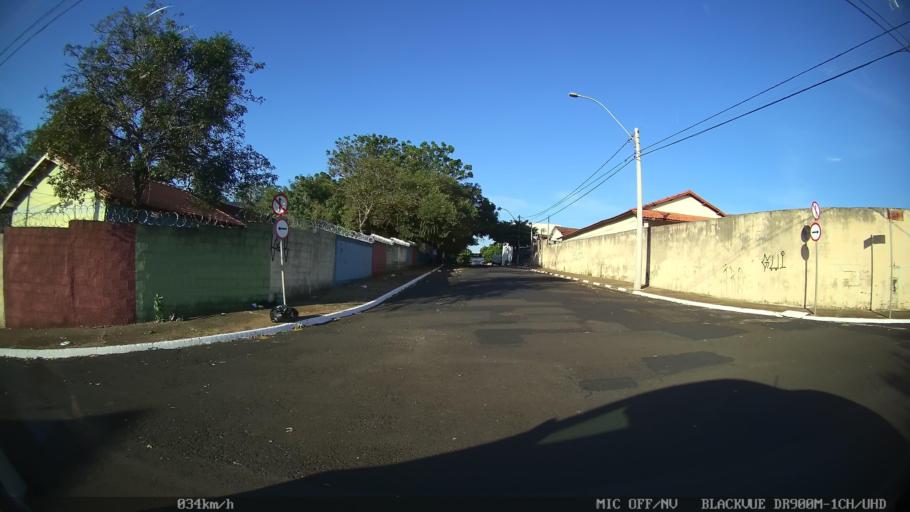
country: BR
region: Sao Paulo
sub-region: Franca
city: Franca
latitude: -20.5215
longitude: -47.3781
